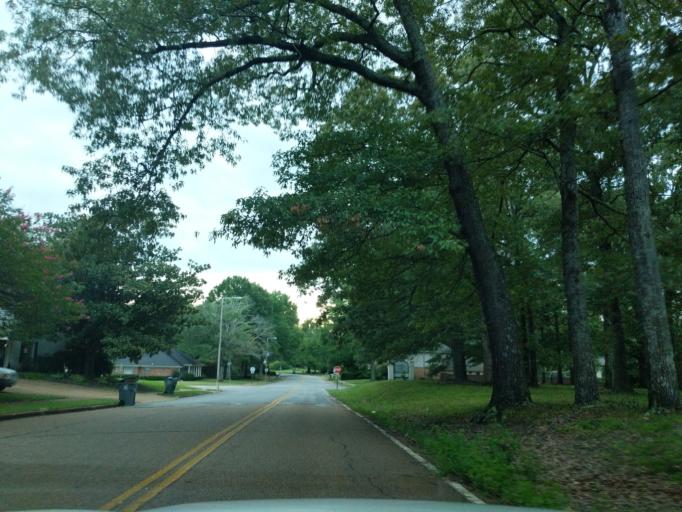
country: US
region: Tennessee
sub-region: Shelby County
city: Germantown
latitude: 35.0777
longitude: -89.8287
